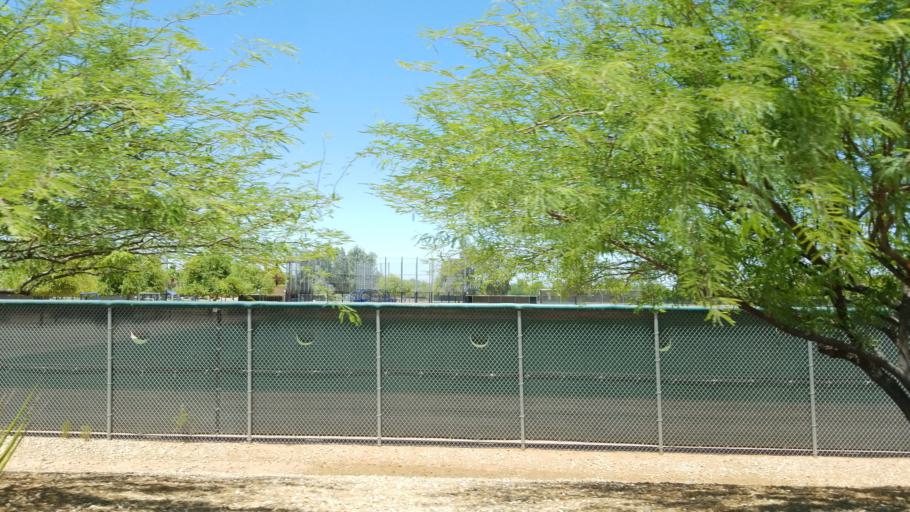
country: US
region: Arizona
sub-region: Maricopa County
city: Tolleson
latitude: 33.5097
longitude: -112.2912
